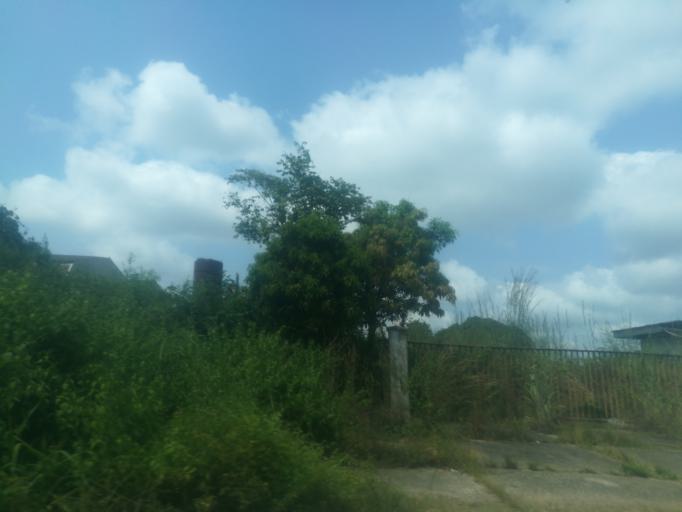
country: NG
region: Oyo
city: Moniya
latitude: 7.5557
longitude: 3.9099
